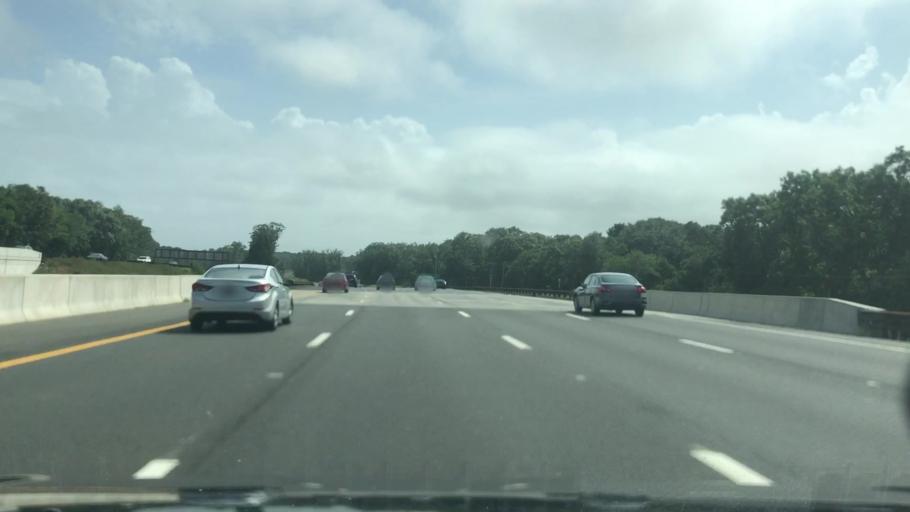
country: US
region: New Jersey
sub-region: Monmouth County
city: Ramtown
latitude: 40.1272
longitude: -74.1257
